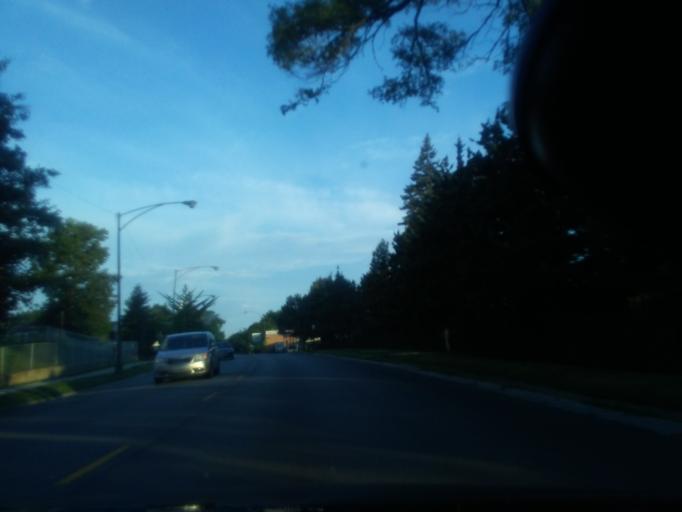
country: US
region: Illinois
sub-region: Cook County
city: Harwood Heights
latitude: 41.9784
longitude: -87.7943
